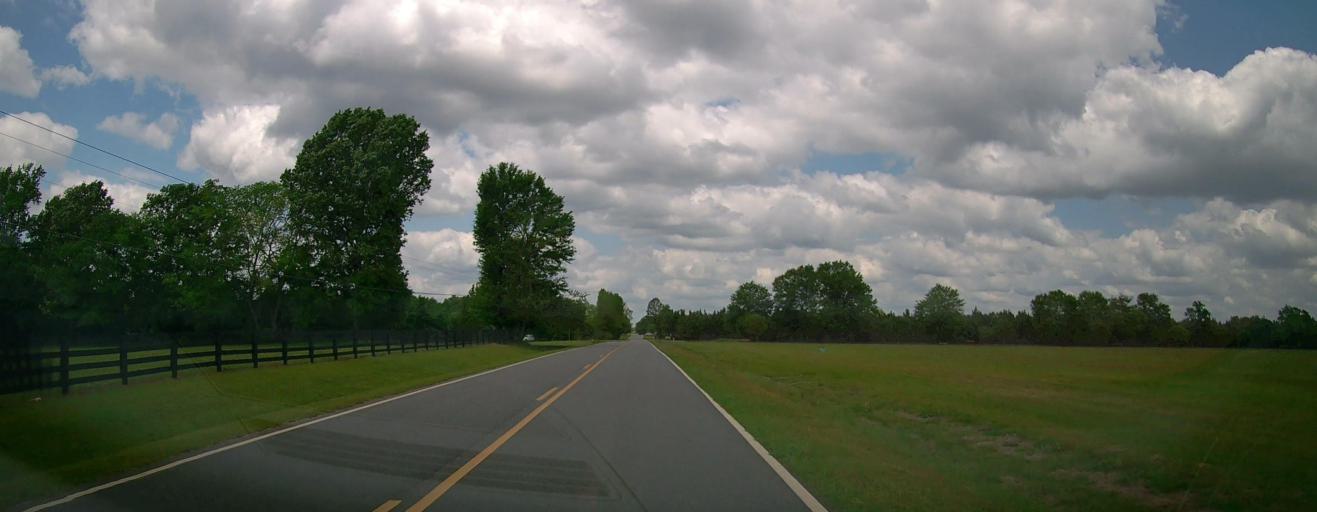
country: US
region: Georgia
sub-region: Laurens County
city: Dublin
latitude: 32.6036
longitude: -82.9594
